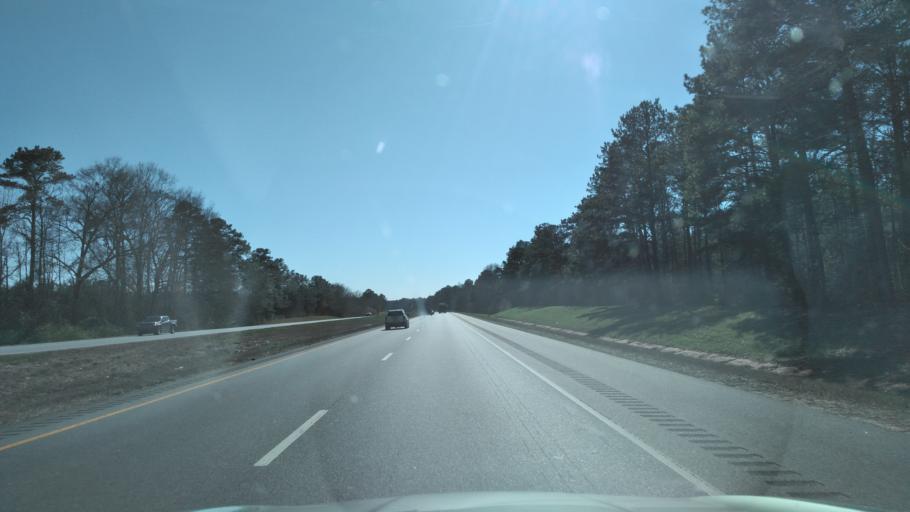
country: US
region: Alabama
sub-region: Butler County
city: Greenville
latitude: 31.9026
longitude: -86.5948
